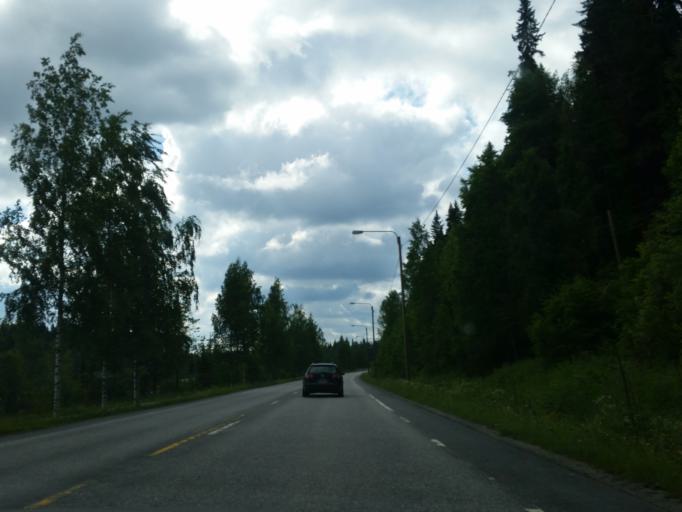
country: FI
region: Northern Savo
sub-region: Kuopio
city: Kuopio
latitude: 62.8454
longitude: 27.5510
